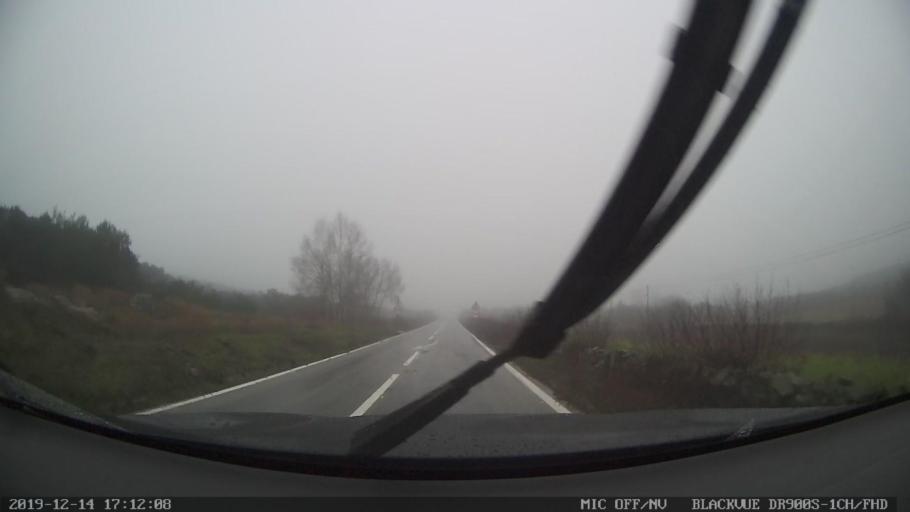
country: PT
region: Vila Real
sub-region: Vila Pouca de Aguiar
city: Vila Pouca de Aguiar
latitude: 41.4910
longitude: -7.6202
